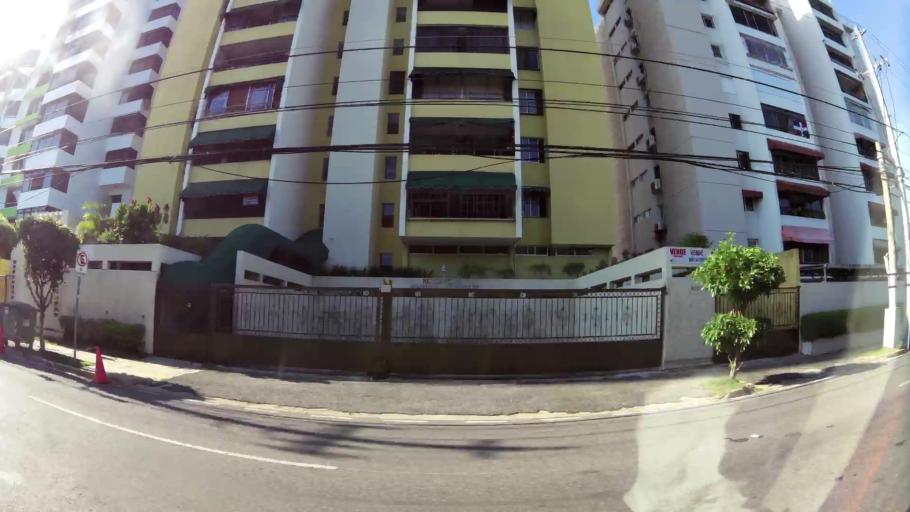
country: DO
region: Nacional
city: Bella Vista
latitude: 18.4403
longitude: -69.9650
